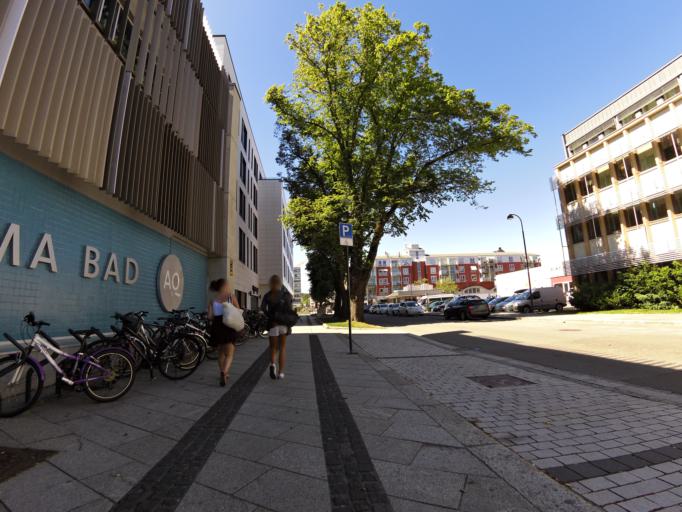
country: NO
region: Vest-Agder
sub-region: Kristiansand
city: Kristiansand
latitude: 58.1472
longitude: 8.0070
